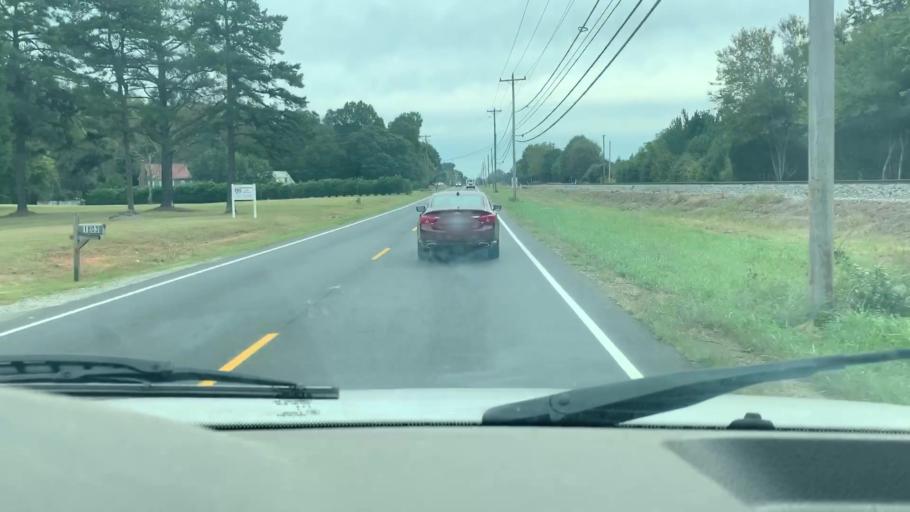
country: US
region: North Carolina
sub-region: Gaston County
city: Davidson
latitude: 35.5259
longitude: -80.8434
